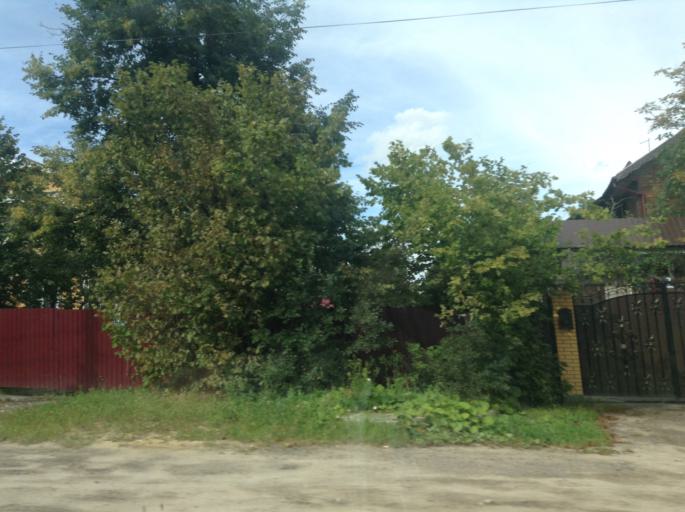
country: RU
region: Moskovskaya
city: Yegor'yevsk
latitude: 55.3595
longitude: 39.1105
